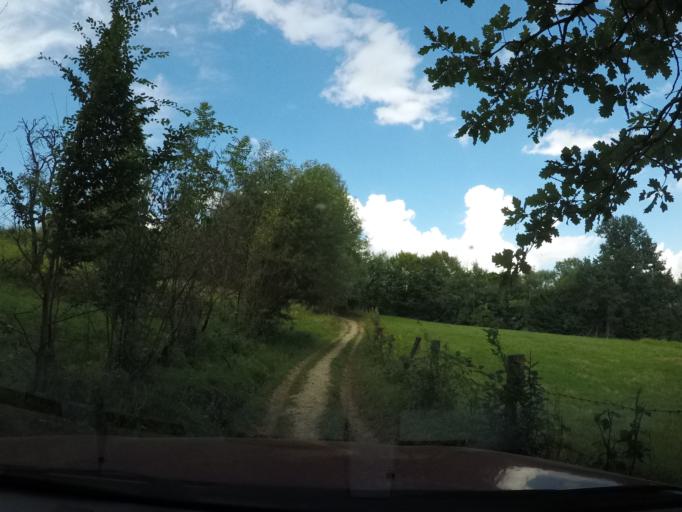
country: UA
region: Zakarpattia
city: Velykyi Bereznyi
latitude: 49.0305
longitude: 22.5911
